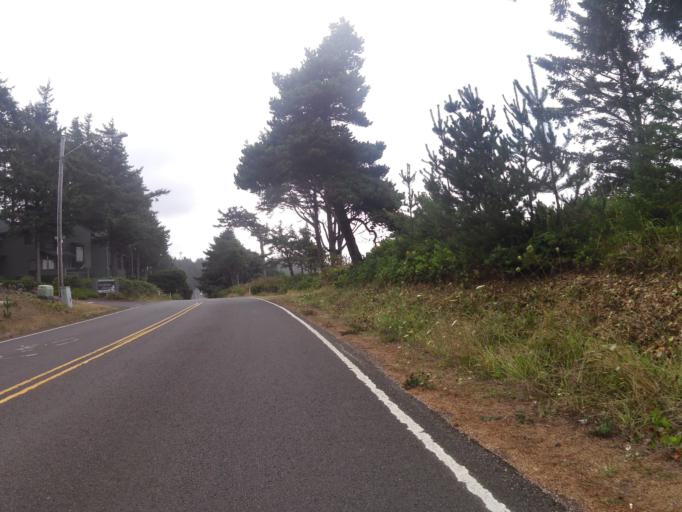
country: US
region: Oregon
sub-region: Lincoln County
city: Newport
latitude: 44.6616
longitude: -124.0570
